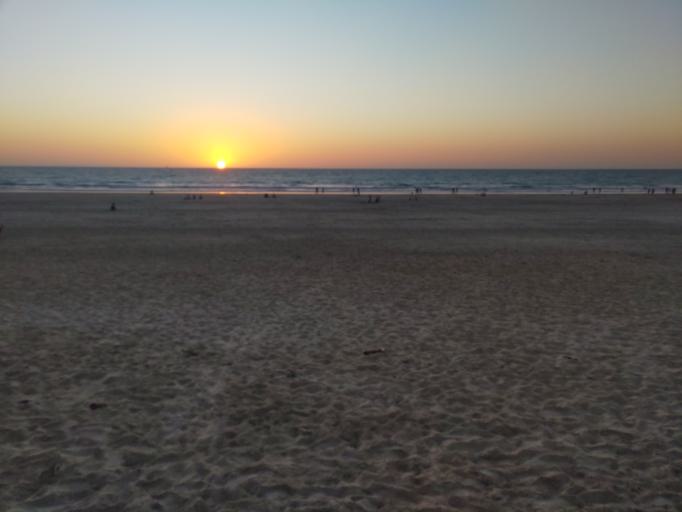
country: AU
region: Western Australia
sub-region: Broome
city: Broome
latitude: -17.9320
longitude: 122.2098
